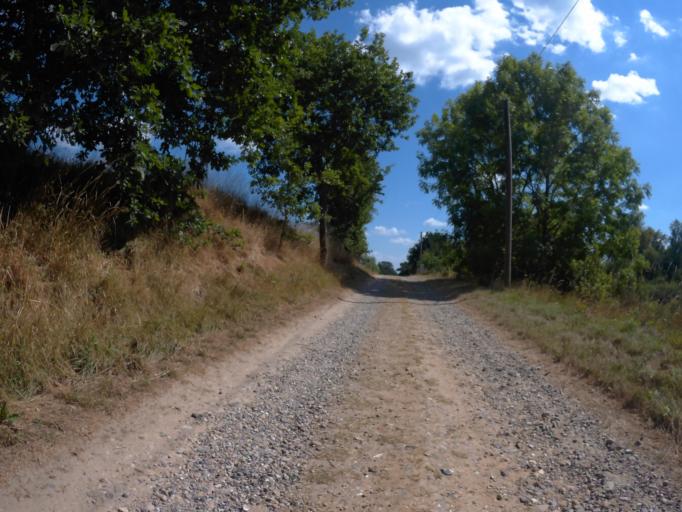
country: DE
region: Schleswig-Holstein
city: Suderstapel
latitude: 54.3608
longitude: 9.2224
